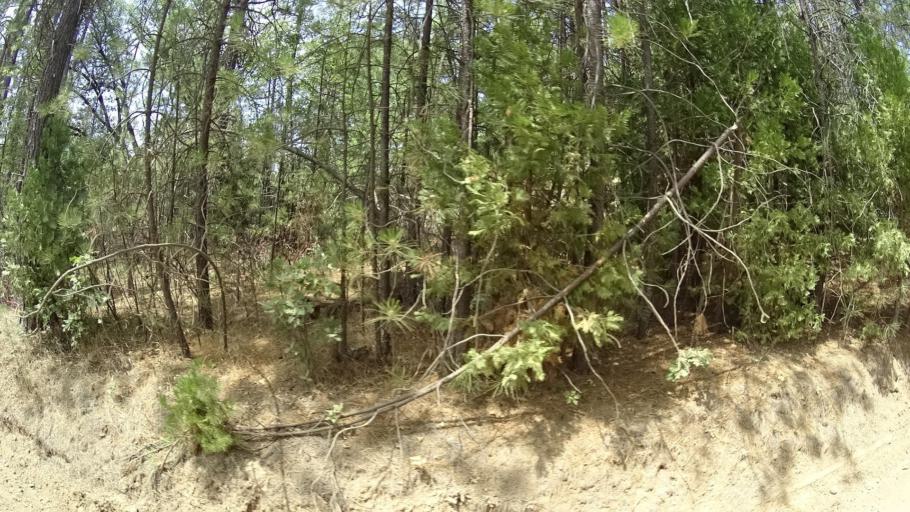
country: US
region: California
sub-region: Mariposa County
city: Midpines
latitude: 37.7413
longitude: -120.0771
